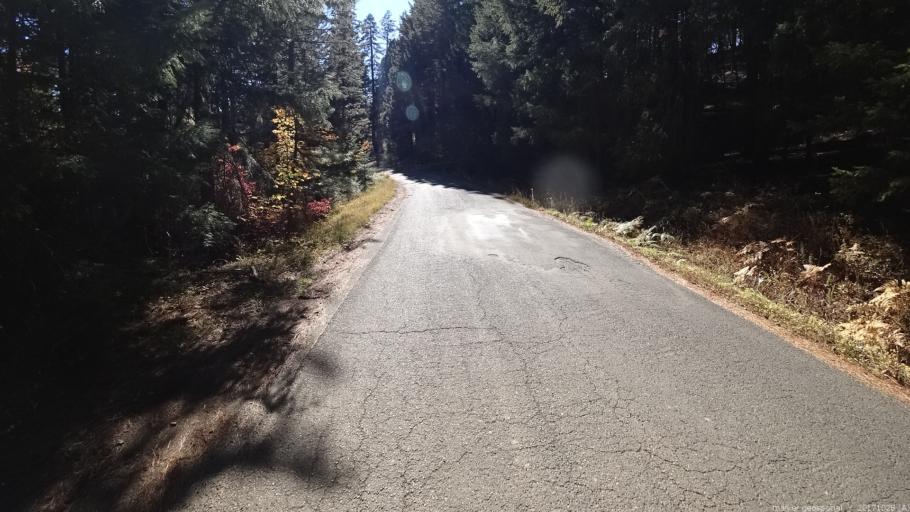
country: US
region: California
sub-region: Trinity County
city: Lewiston
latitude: 40.8230
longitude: -122.6632
